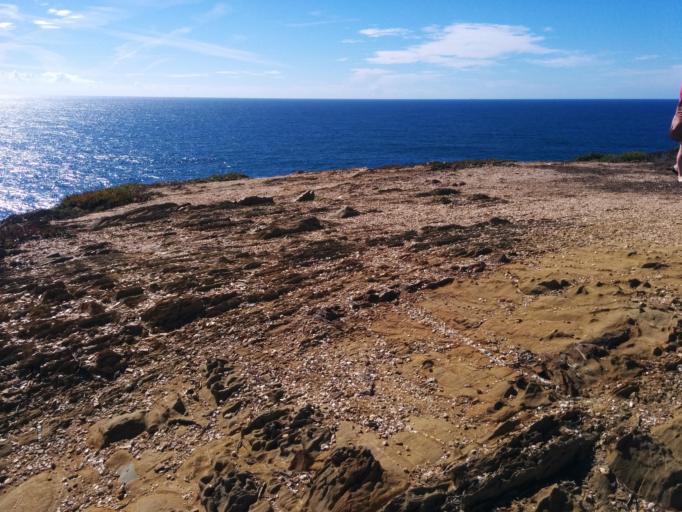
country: PT
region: Beja
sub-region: Odemira
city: Vila Nova de Milfontes
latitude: 37.5978
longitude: -8.8183
